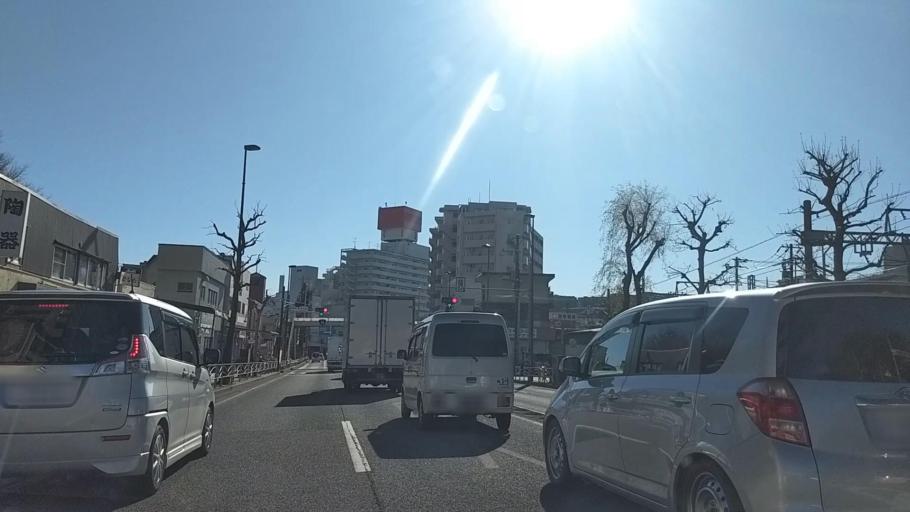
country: JP
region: Kanagawa
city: Zushi
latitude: 35.3178
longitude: 139.6233
